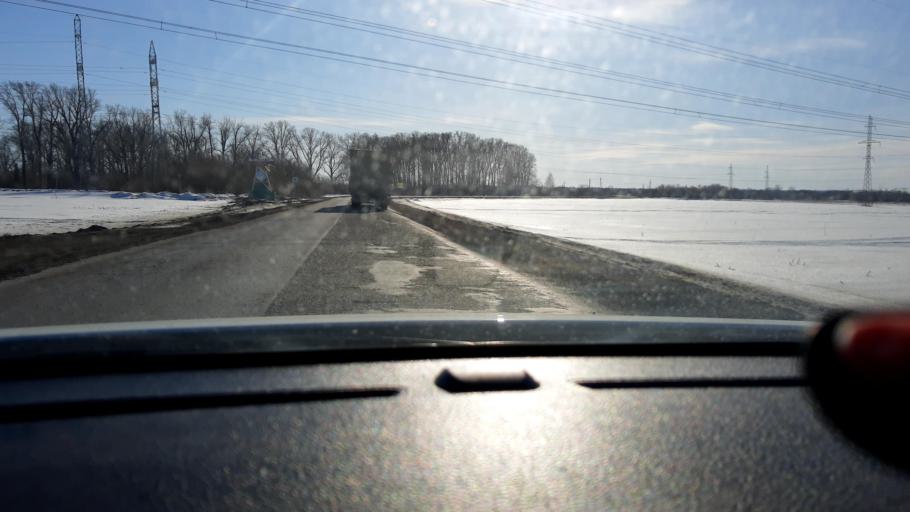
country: RU
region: Bashkortostan
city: Avdon
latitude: 54.4340
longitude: 55.8263
